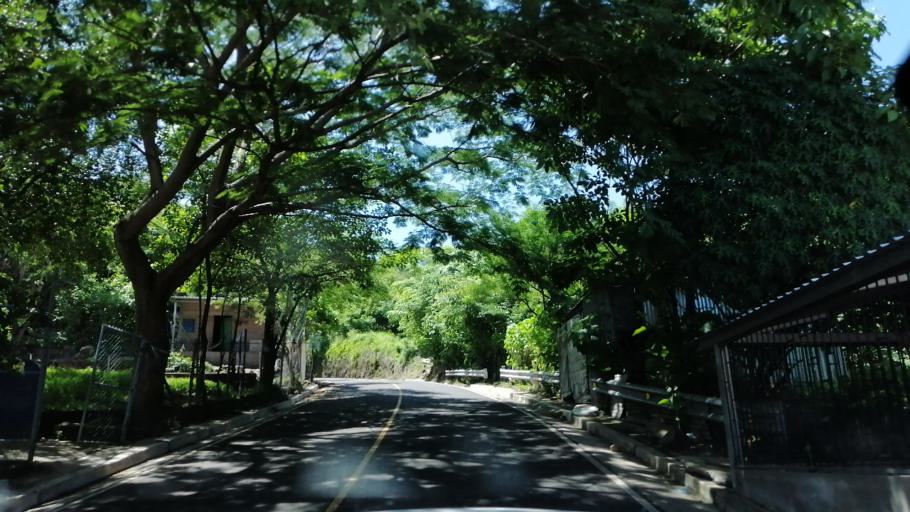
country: SV
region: San Miguel
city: Sesori
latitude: 13.8075
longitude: -88.4020
